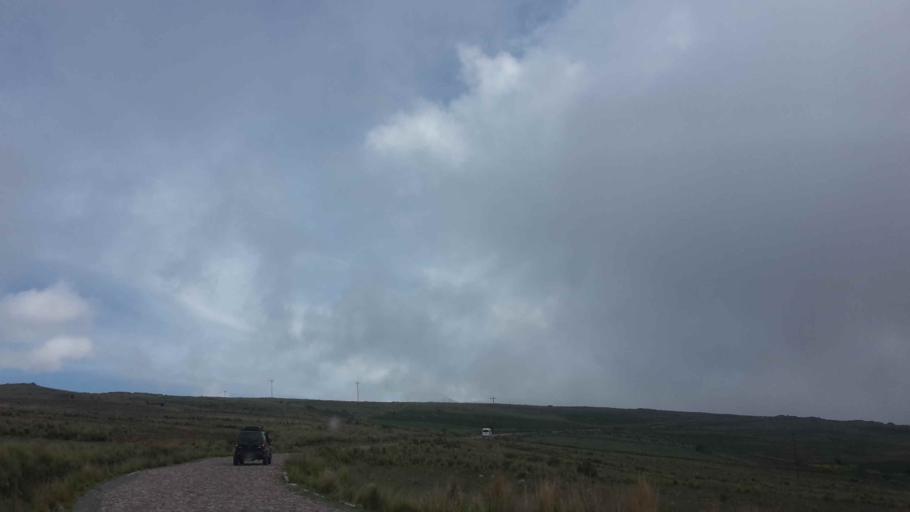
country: BO
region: Cochabamba
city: Cochabamba
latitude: -17.3281
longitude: -66.0795
